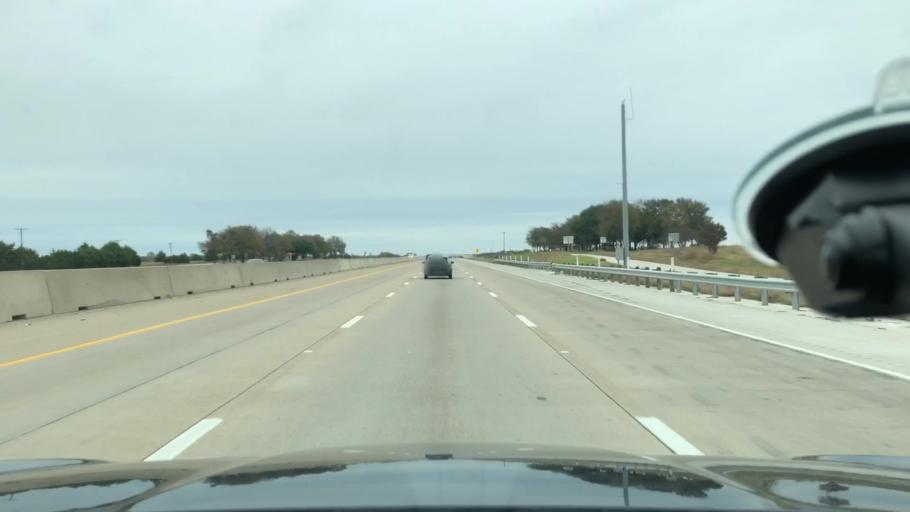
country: US
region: Texas
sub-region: Ellis County
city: Nash
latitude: 32.2791
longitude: -96.8689
